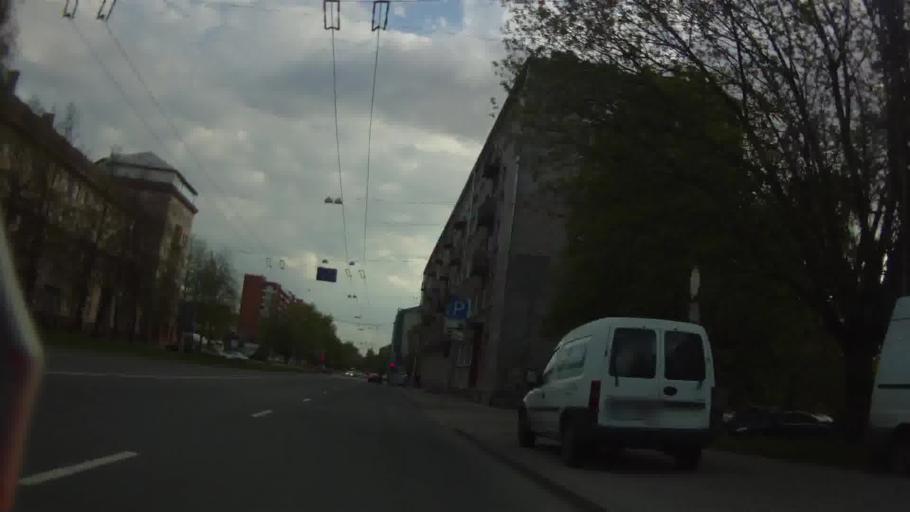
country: LV
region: Riga
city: Riga
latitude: 56.9731
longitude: 24.1349
